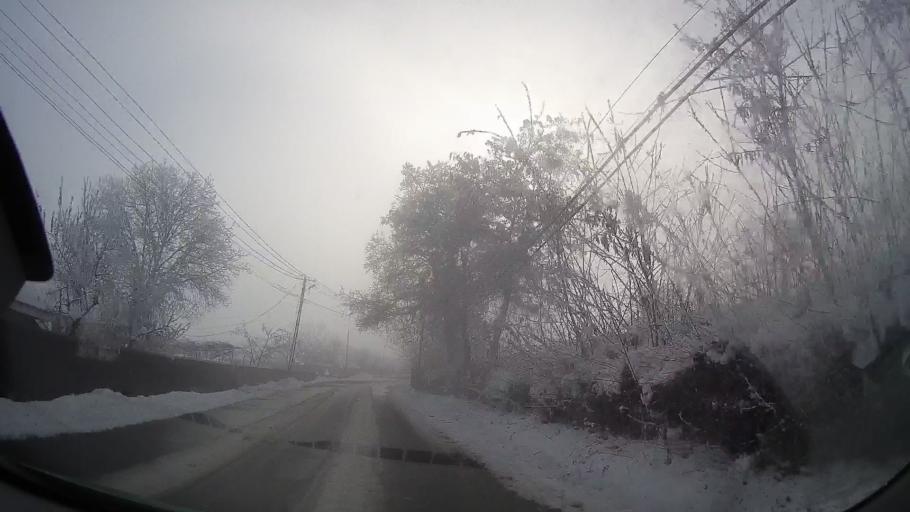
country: RO
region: Iasi
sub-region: Comuna Valea Seaca
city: Topile
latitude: 47.2547
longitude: 26.6665
